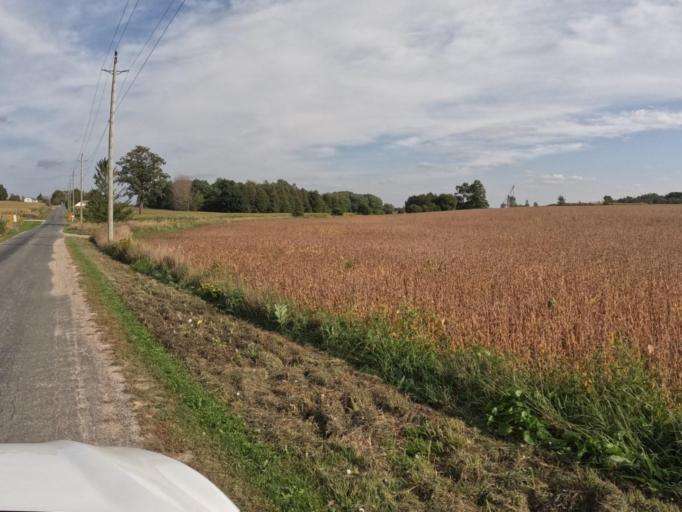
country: CA
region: Ontario
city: Waterloo
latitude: 43.6071
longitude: -80.5482
